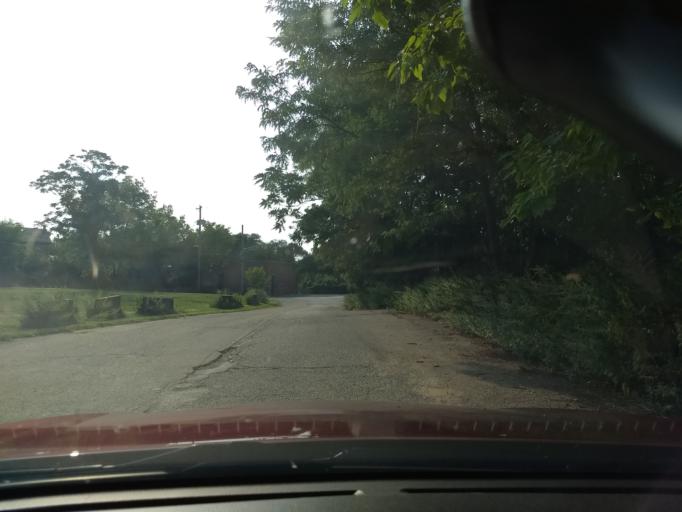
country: US
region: Pennsylvania
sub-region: Allegheny County
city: Aspinwall
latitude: 40.4698
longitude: -79.9009
